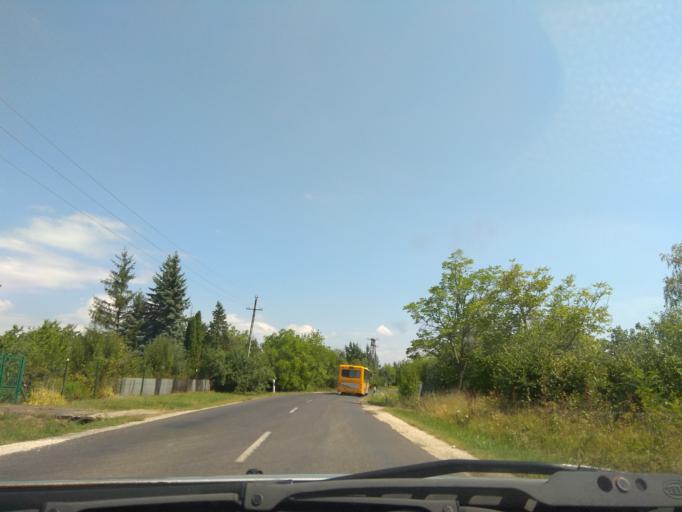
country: HU
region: Borsod-Abauj-Zemplen
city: Harsany
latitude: 48.0303
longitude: 20.7673
